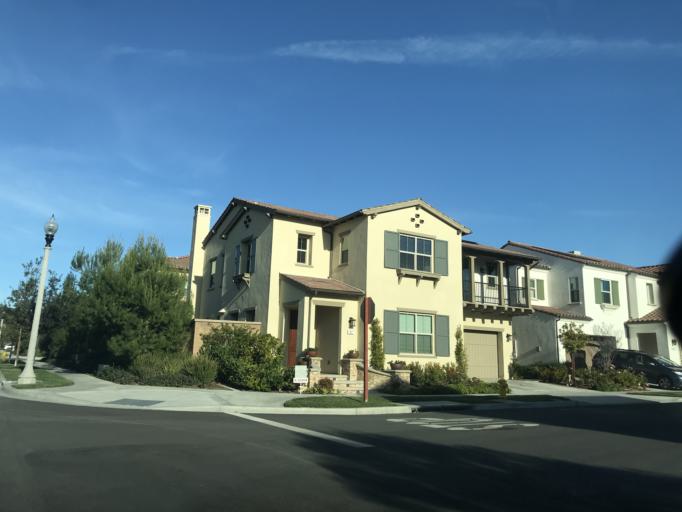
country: US
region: California
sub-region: Orange County
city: North Tustin
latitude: 33.7139
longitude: -117.7415
